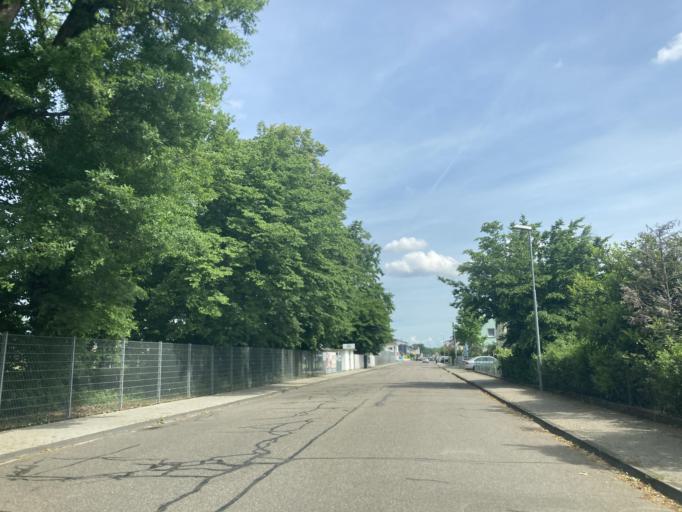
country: DE
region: Baden-Wuerttemberg
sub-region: Karlsruhe Region
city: Waghausel
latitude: 49.2436
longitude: 8.5358
